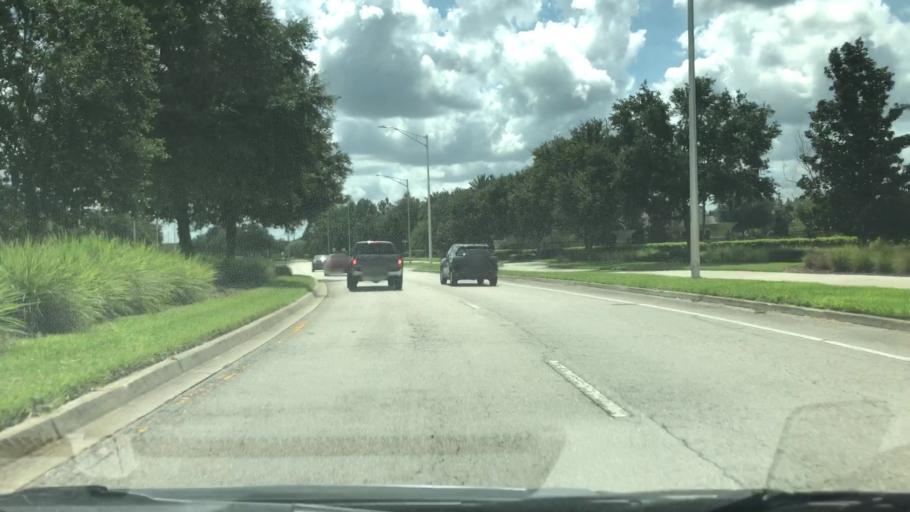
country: US
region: Florida
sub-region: Saint Johns County
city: Fruit Cove
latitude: 30.1299
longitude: -81.5423
